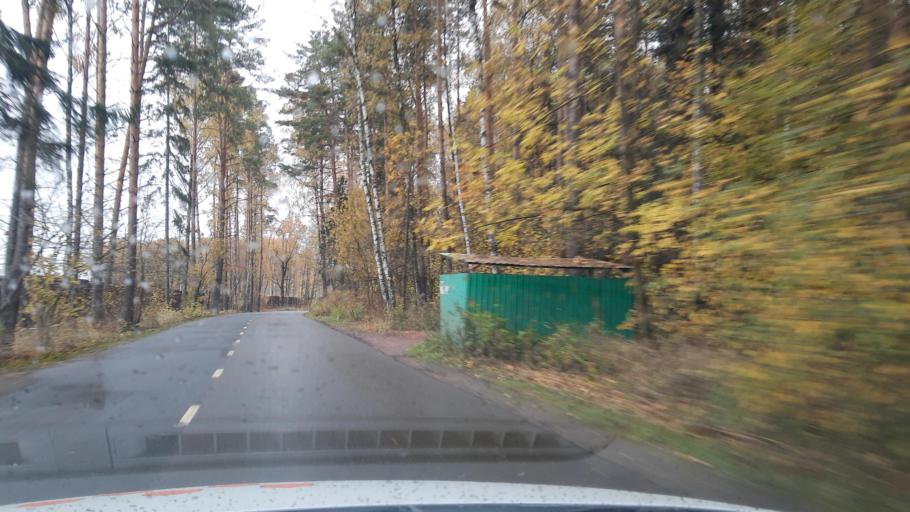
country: RU
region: Moskovskaya
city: Shcherbinka
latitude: 55.5343
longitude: 37.5671
